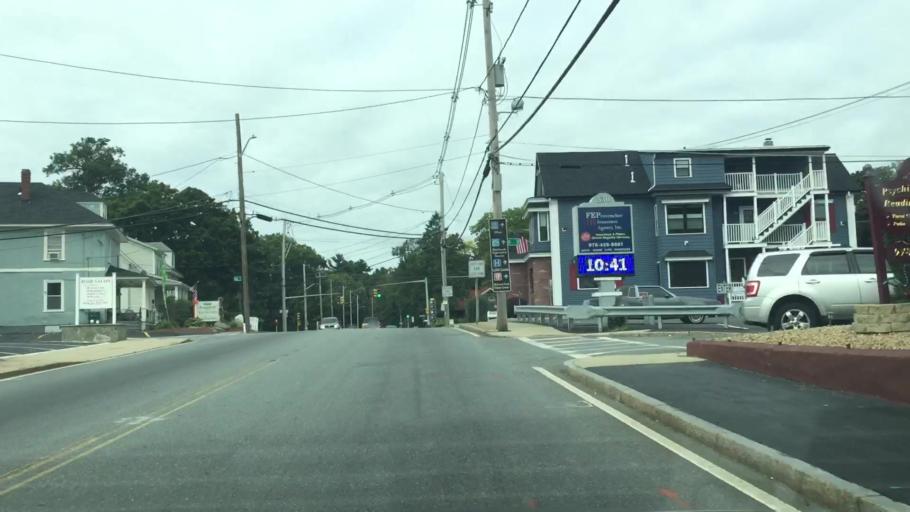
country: US
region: Massachusetts
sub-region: Middlesex County
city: Lowell
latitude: 42.6319
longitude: -71.2853
